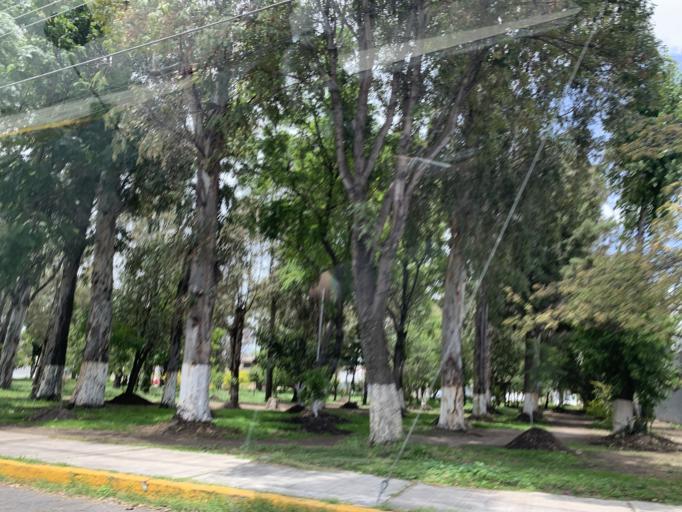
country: MX
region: Puebla
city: Puebla
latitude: 19.0672
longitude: -98.2148
